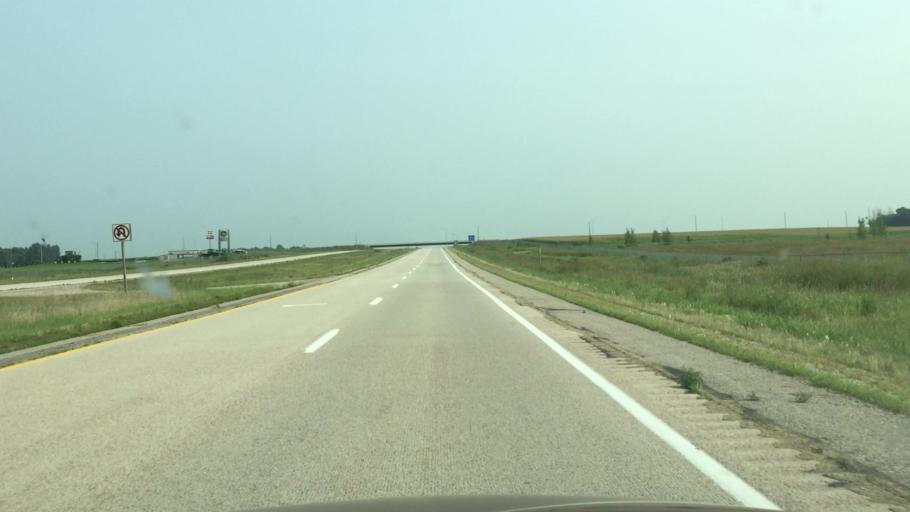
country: US
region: Iowa
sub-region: Osceola County
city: Sibley
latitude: 43.3973
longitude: -95.7171
